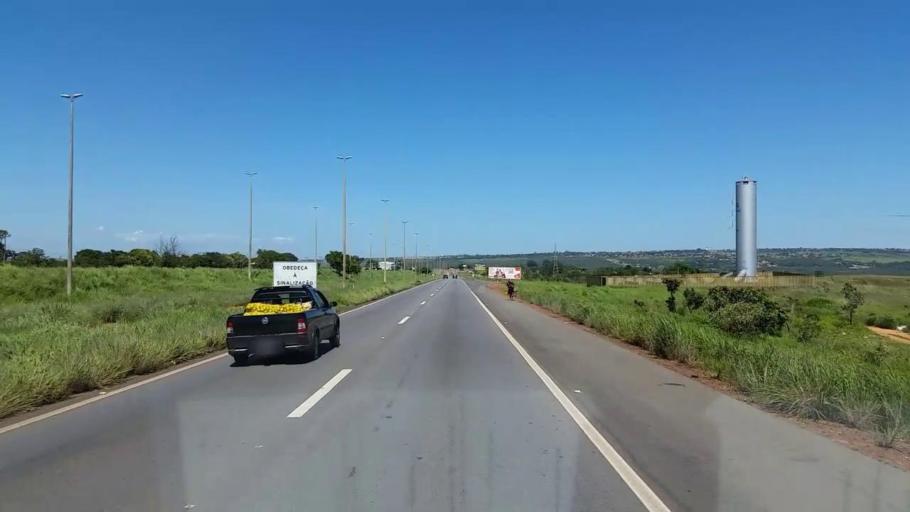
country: BR
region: Federal District
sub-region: Brasilia
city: Brasilia
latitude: -15.7937
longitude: -48.2020
